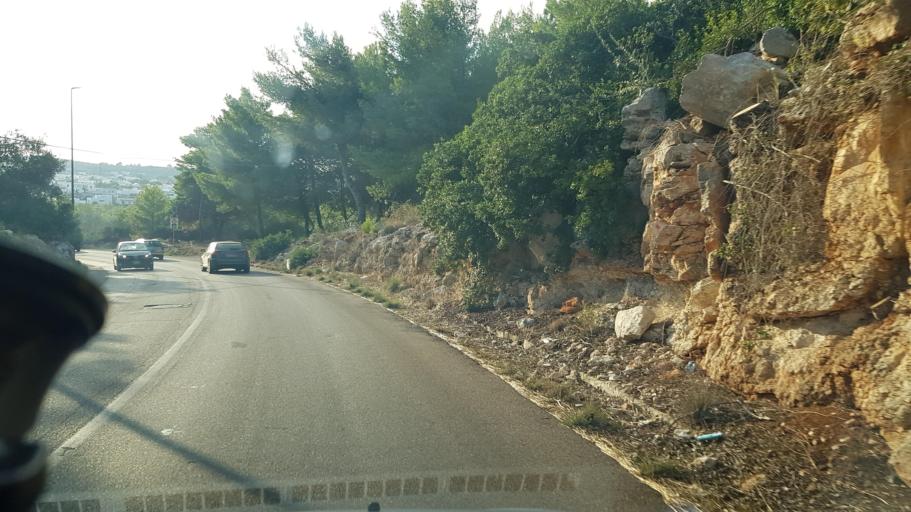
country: IT
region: Apulia
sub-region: Provincia di Lecce
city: Leuca
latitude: 39.8004
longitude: 18.3665
